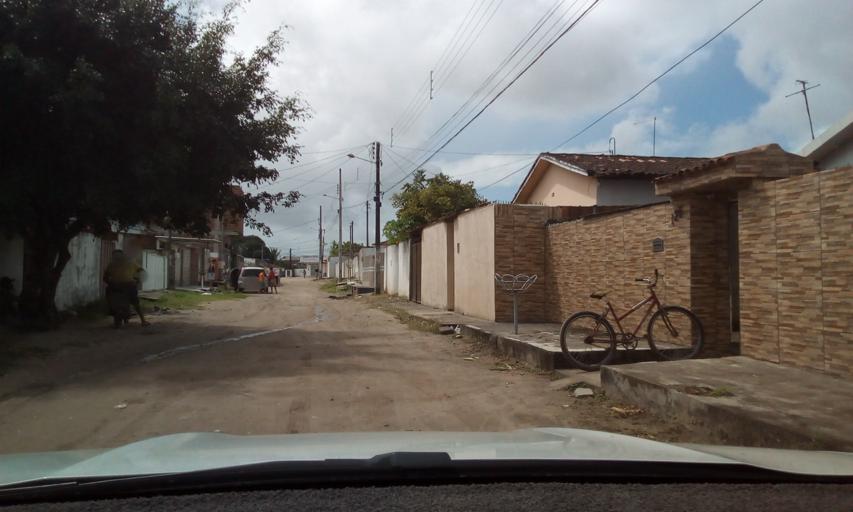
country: BR
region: Paraiba
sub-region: Santa Rita
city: Santa Rita
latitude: -7.1420
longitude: -34.9665
